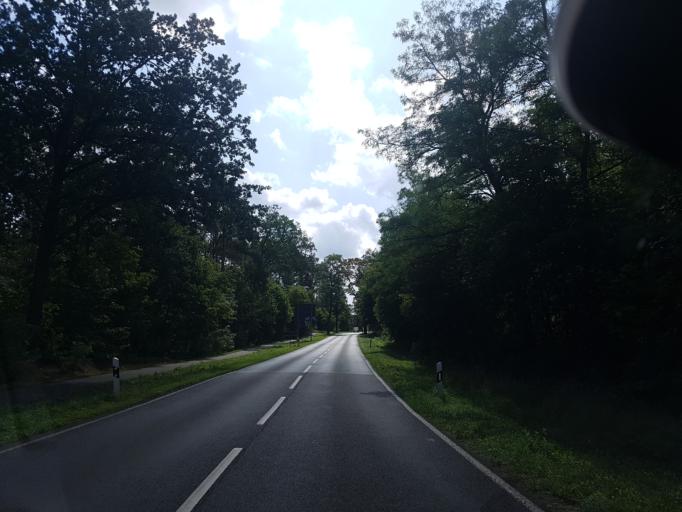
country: DE
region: Brandenburg
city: Gross Kreutz
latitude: 52.3287
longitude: 12.7304
